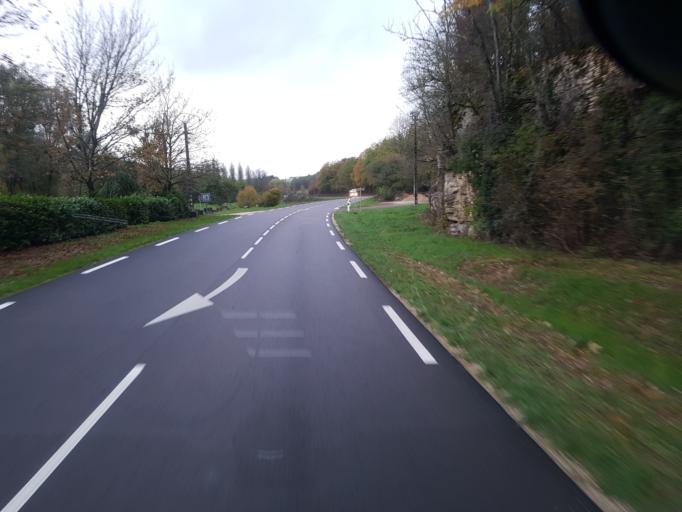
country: FR
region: Bourgogne
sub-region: Departement de la Cote-d'Or
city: Chatillon-sur-Seine
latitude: 47.6713
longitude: 4.7253
